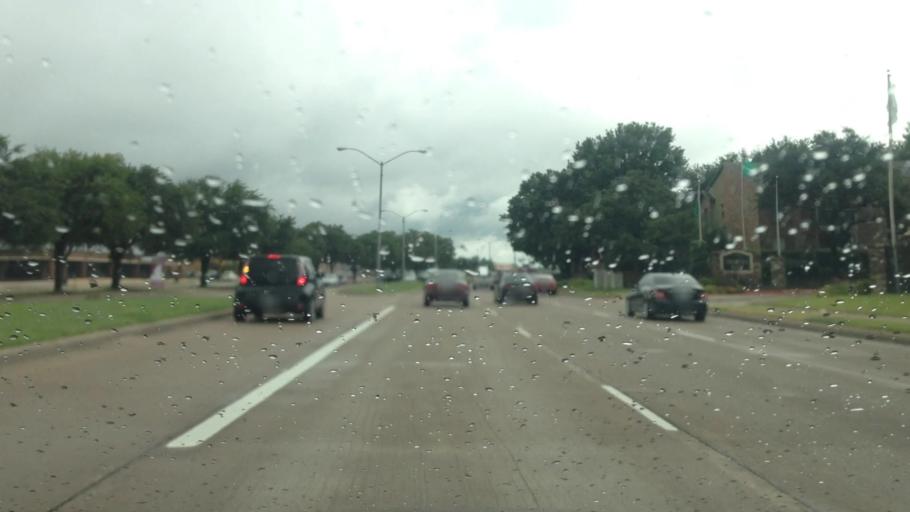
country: US
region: Texas
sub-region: Tarrant County
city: Edgecliff Village
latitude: 32.6699
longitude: -97.4000
